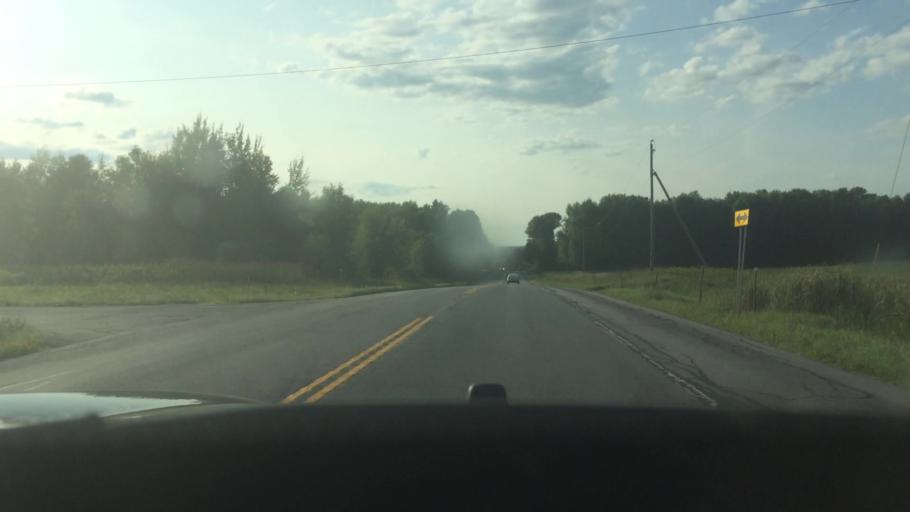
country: US
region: New York
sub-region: St. Lawrence County
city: Canton
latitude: 44.6039
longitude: -75.2028
